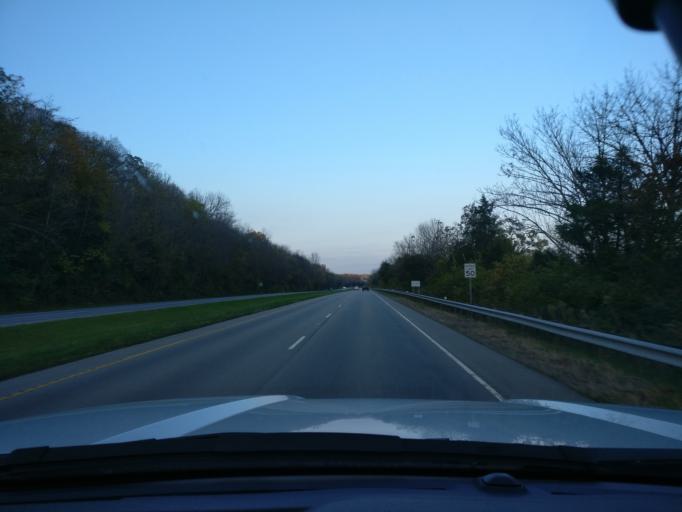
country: US
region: Ohio
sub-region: Warren County
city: Waynesville
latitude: 39.5188
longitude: -84.0970
